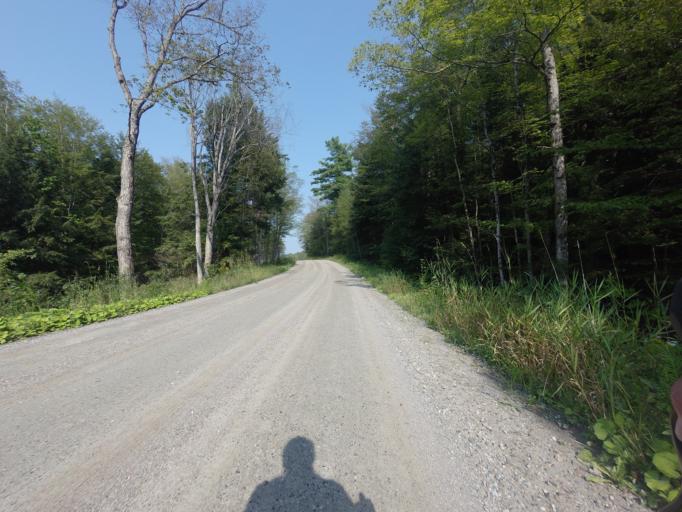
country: CA
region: Ontario
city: Perth
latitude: 44.7867
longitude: -76.7722
